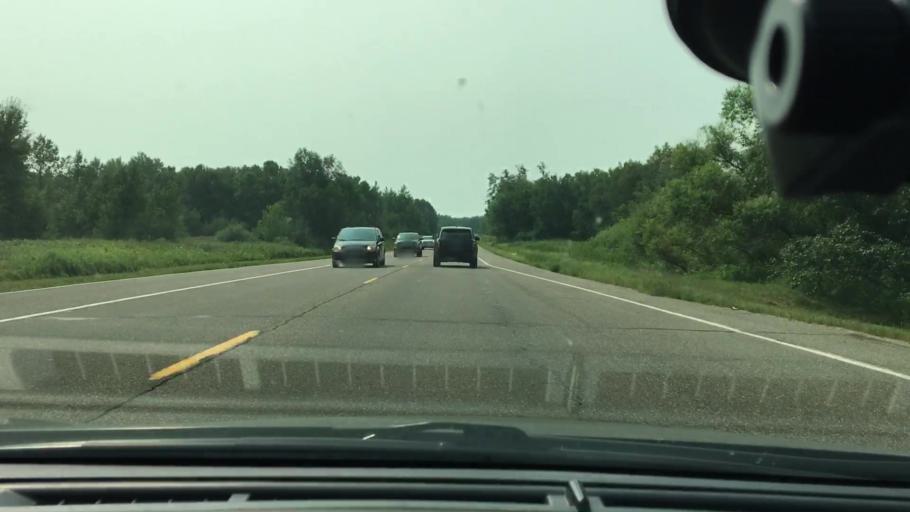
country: US
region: Minnesota
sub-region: Crow Wing County
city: Brainerd
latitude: 46.3937
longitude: -94.2233
